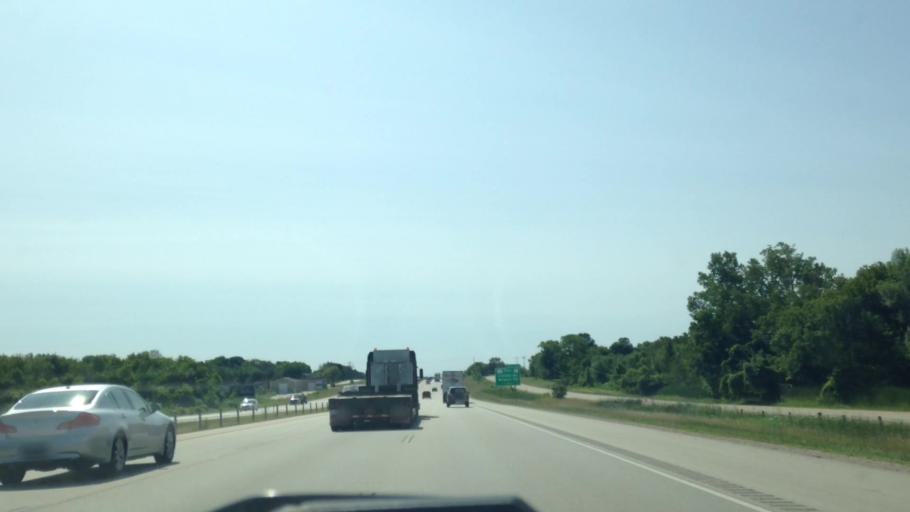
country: US
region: Wisconsin
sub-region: Washington County
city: Richfield
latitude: 43.2297
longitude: -88.1677
